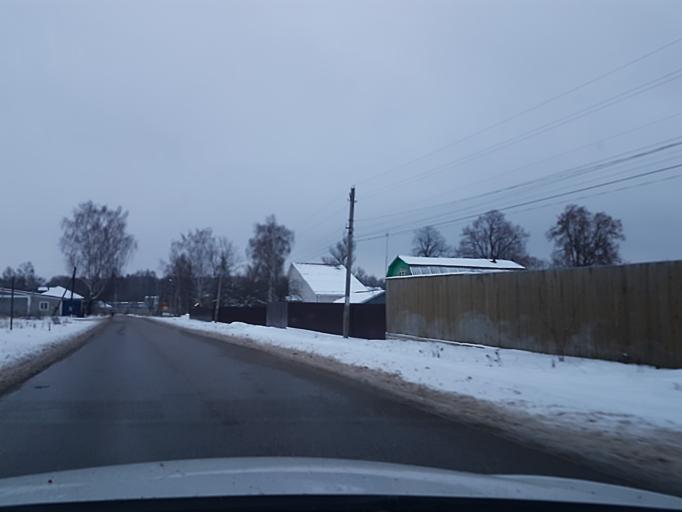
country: RU
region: Tverskaya
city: Novozavidovskiy
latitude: 56.5544
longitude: 36.4289
